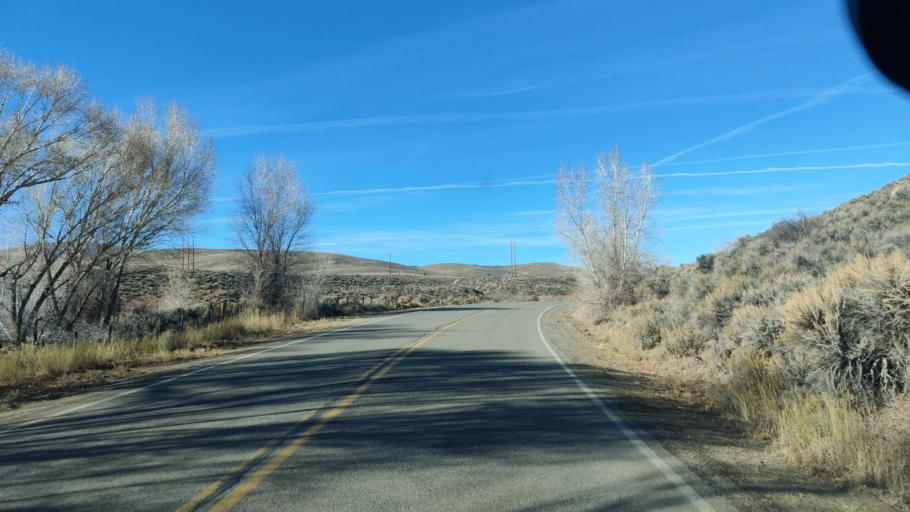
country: US
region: Colorado
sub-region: Gunnison County
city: Gunnison
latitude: 38.5603
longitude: -106.9557
